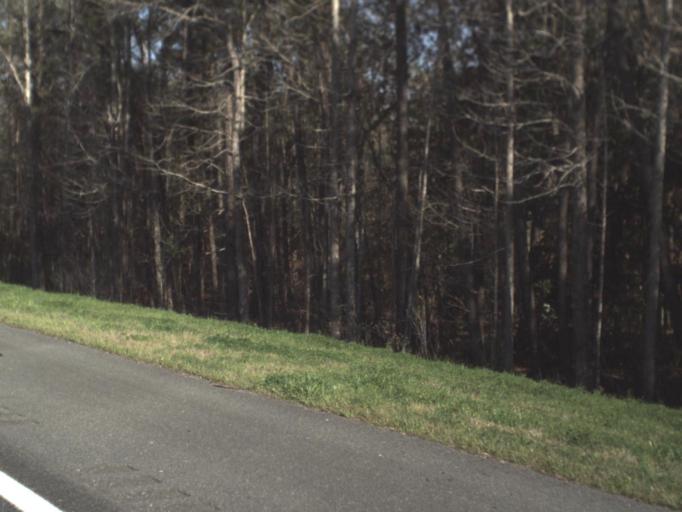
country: US
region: Florida
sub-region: Gadsden County
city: Midway
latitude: 30.5082
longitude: -84.4652
